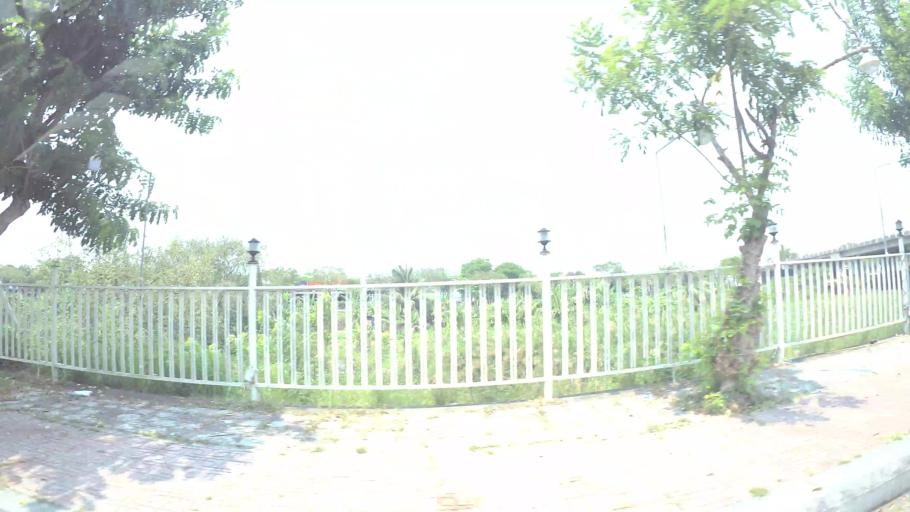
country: VN
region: Da Nang
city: Cam Le
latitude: 16.0168
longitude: 108.2120
